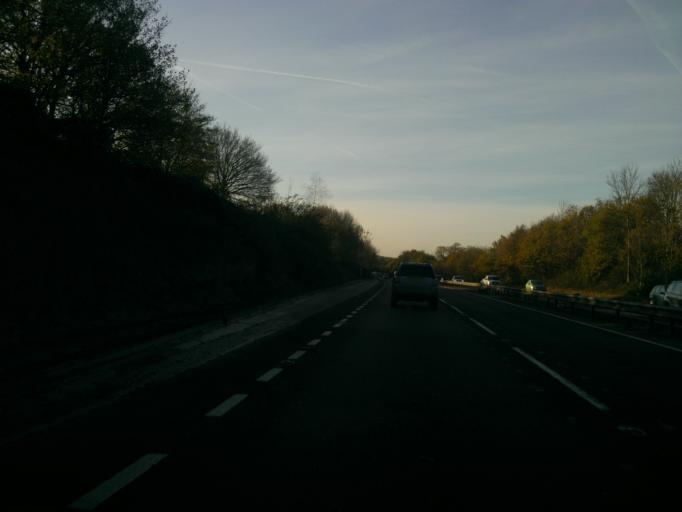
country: GB
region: England
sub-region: Essex
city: Great Horkesley
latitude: 51.9161
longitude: 0.8749
